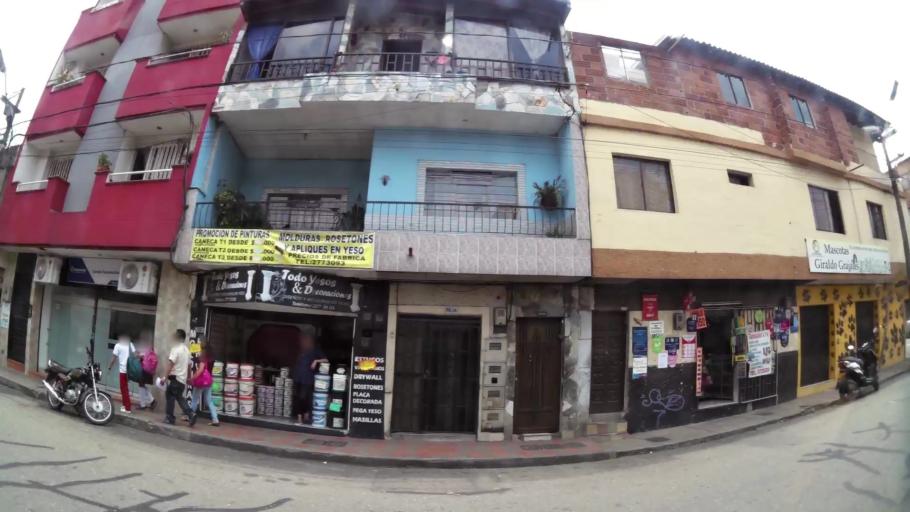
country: CO
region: Antioquia
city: Itagui
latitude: 6.1751
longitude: -75.6066
